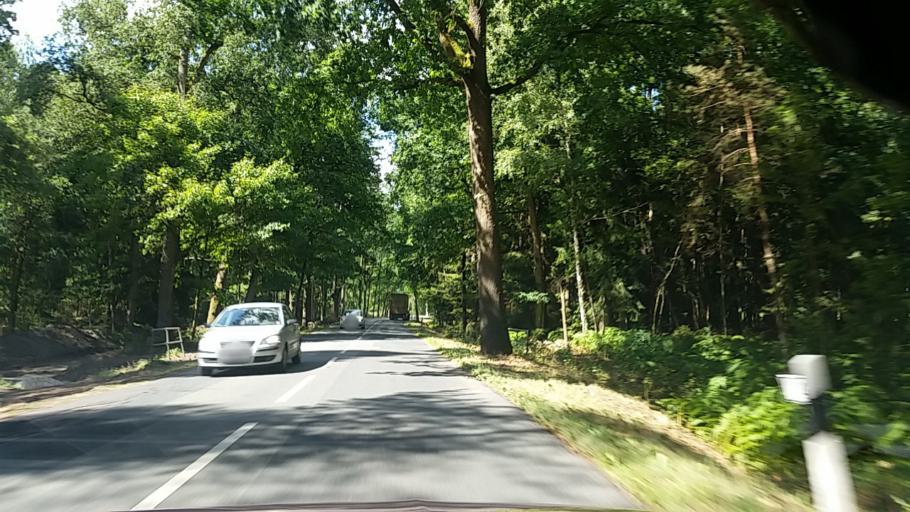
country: DE
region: Lower Saxony
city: Hankensbuttel
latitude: 52.7057
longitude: 10.6455
